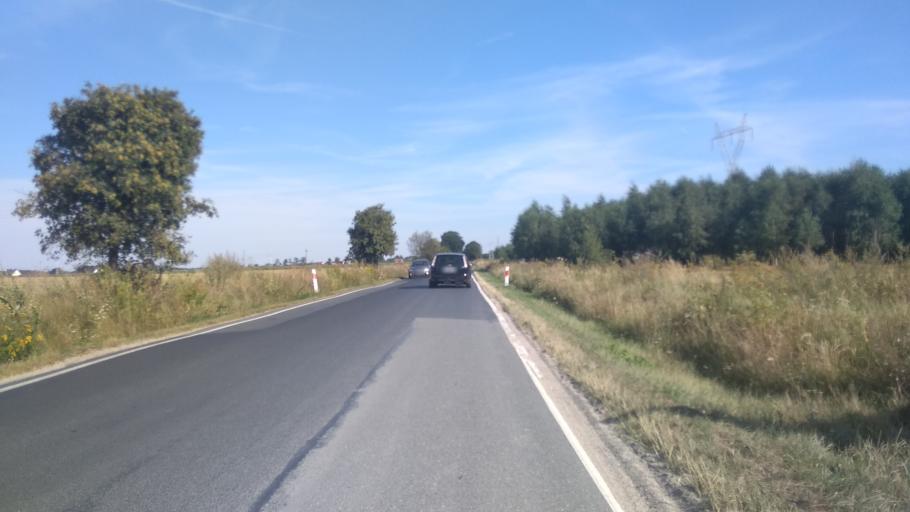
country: PL
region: Kujawsko-Pomorskie
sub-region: Powiat bydgoski
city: Osielsko
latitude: 53.2179
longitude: 18.1382
